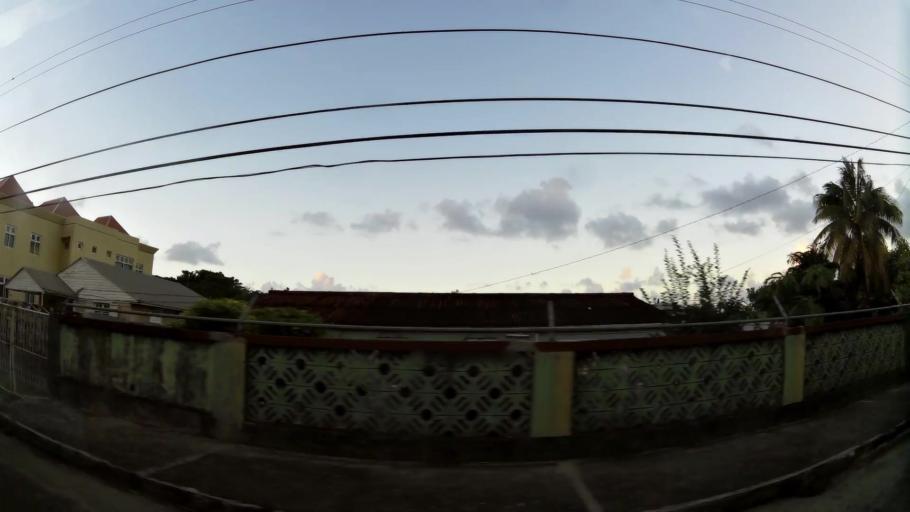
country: AG
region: Saint John
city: Saint John's
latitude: 17.1237
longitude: -61.8370
